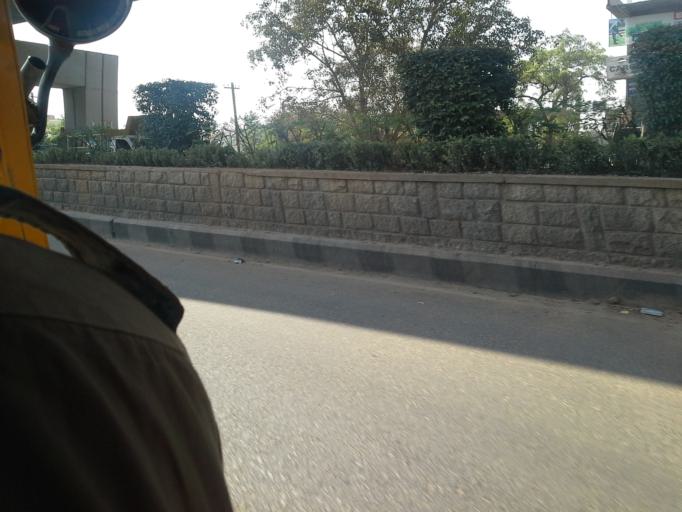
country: IN
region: Telangana
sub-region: Hyderabad
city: Hyderabad
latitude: 17.3718
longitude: 78.4294
